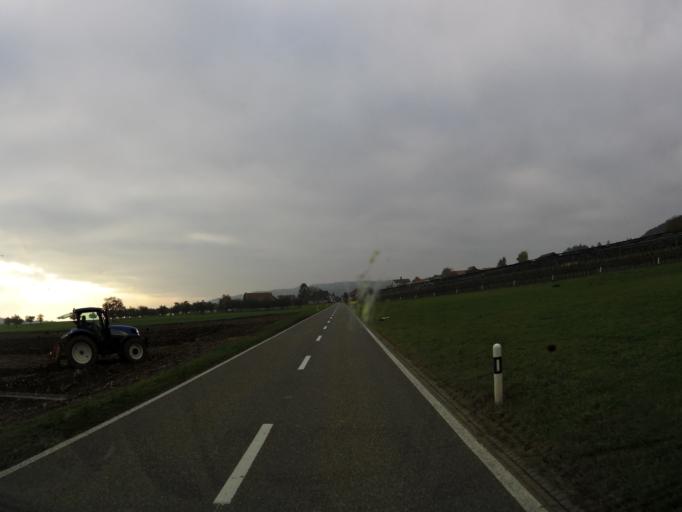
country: CH
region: Thurgau
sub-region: Frauenfeld District
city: Pfyn
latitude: 47.6237
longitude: 8.9459
